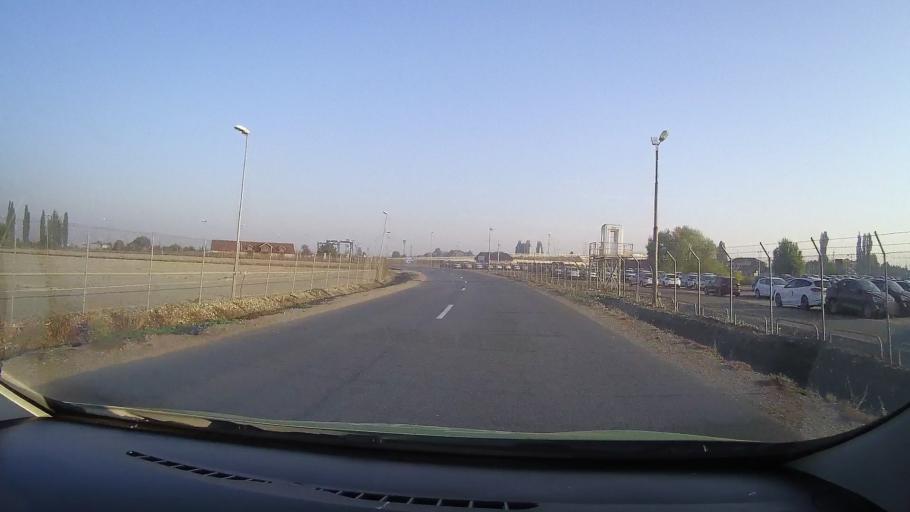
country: RO
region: Arad
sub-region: Comuna Curtici
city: Curtici
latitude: 46.3350
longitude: 21.2976
